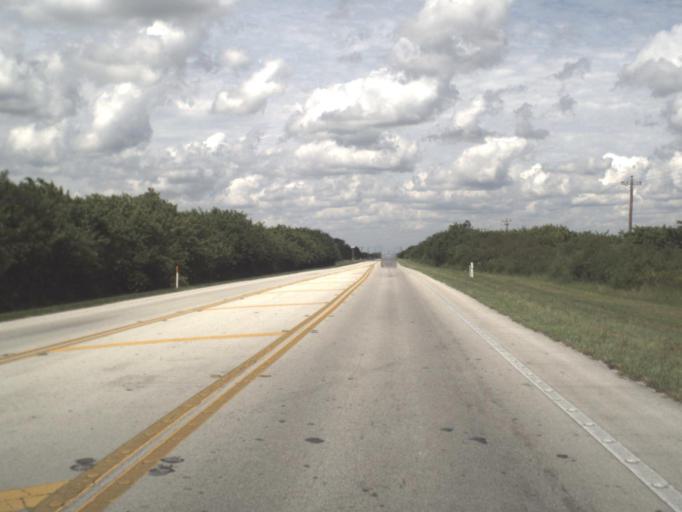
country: US
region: Florida
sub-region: Collier County
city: Immokalee
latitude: 26.4756
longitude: -81.4345
